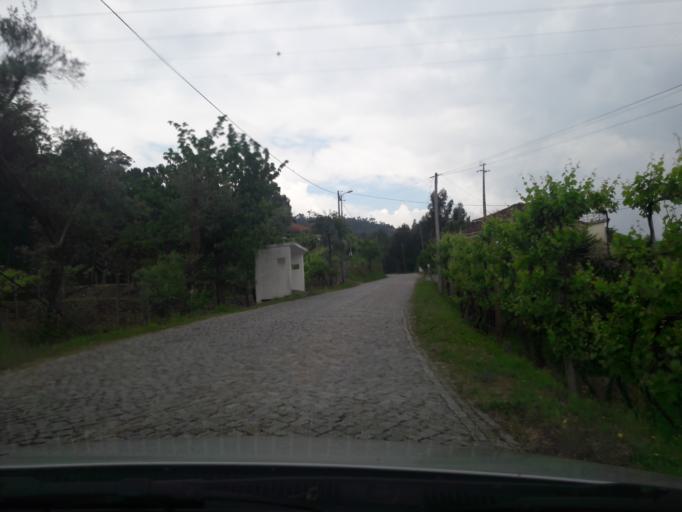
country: PT
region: Porto
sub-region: Amarante
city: Teloes
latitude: 41.3366
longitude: -8.0701
